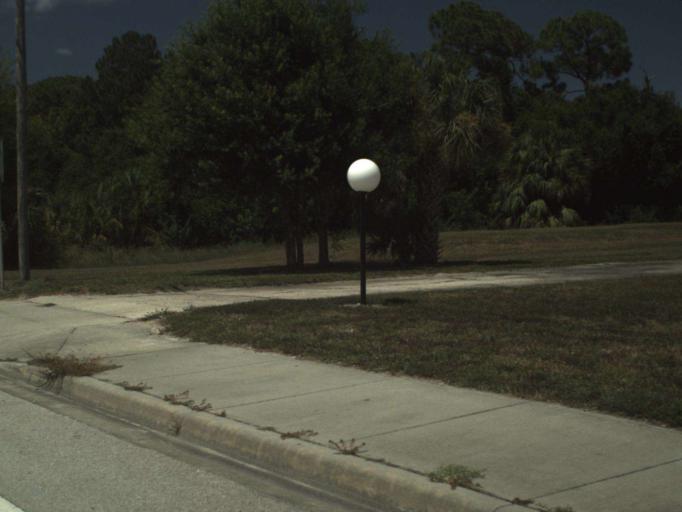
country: US
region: Florida
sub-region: Saint Lucie County
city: White City
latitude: 27.3701
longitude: -80.3257
